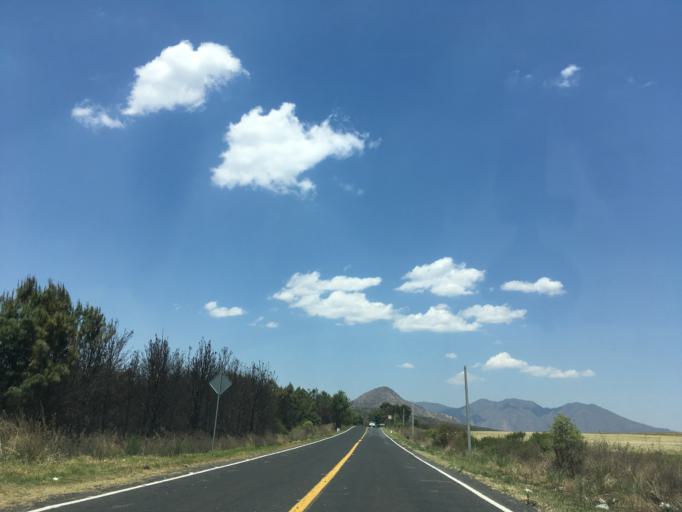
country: MX
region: Mexico
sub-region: Chalco
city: Zopoco
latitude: 19.7911
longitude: -102.0242
